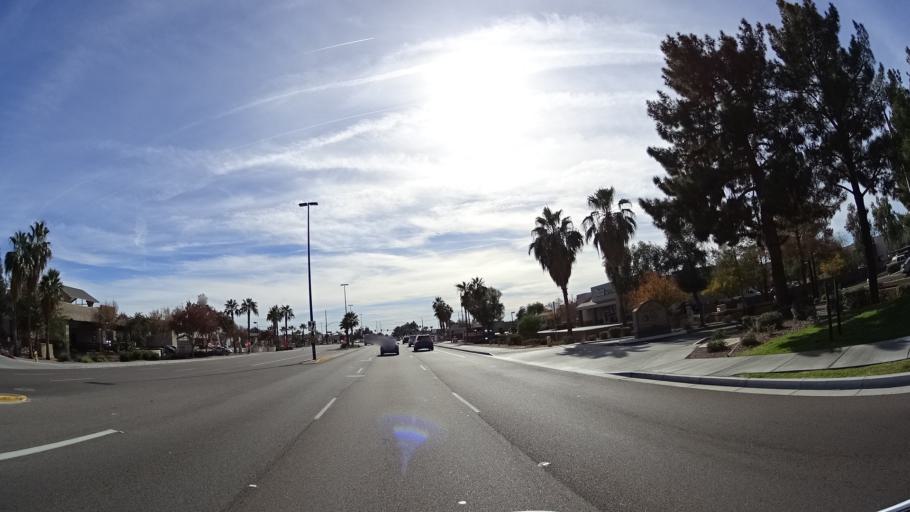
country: US
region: Arizona
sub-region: Maricopa County
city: Gilbert
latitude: 33.3667
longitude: -111.7900
